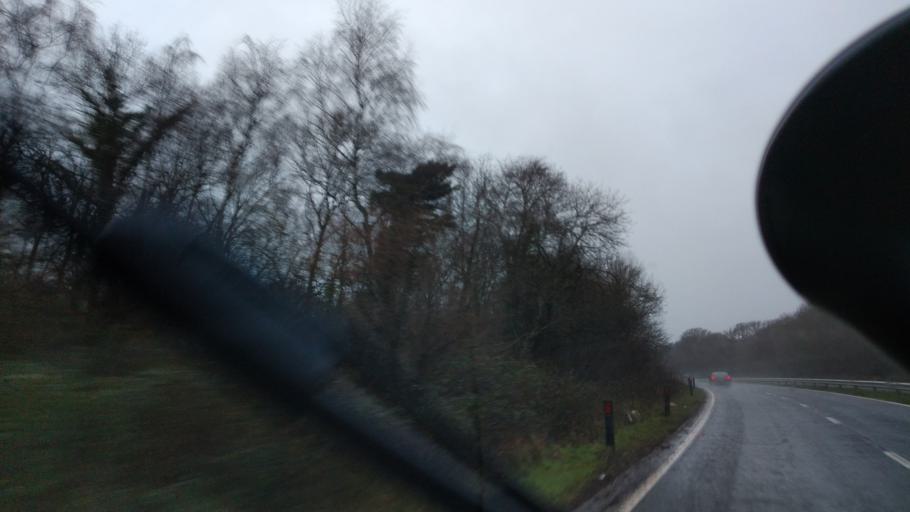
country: GB
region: England
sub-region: West Sussex
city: Goring-by-Sea
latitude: 50.8409
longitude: -0.4377
